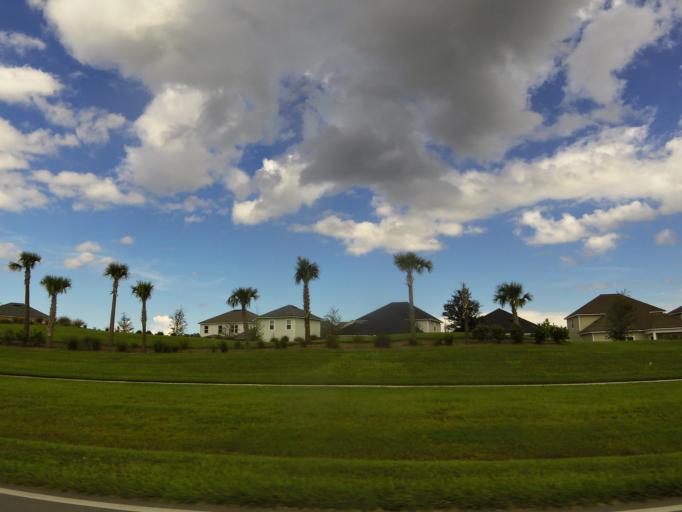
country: US
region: Florida
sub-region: Saint Johns County
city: Saint Augustine
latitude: 29.9237
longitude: -81.4961
